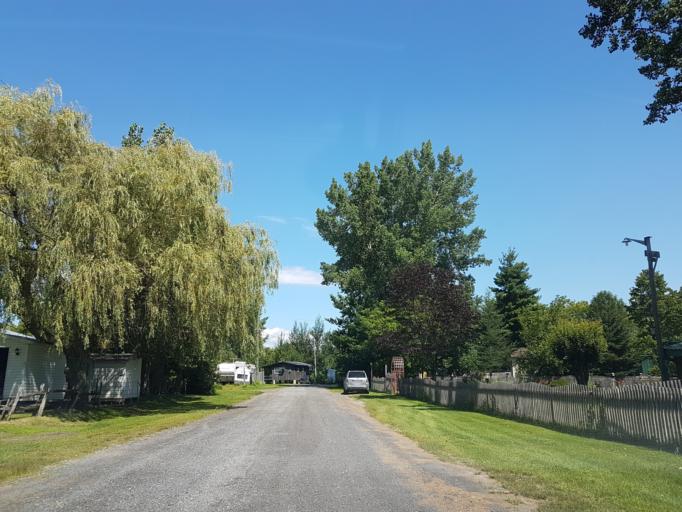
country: CA
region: Quebec
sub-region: Mauricie
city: Pierreville
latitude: 46.1602
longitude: -72.7547
